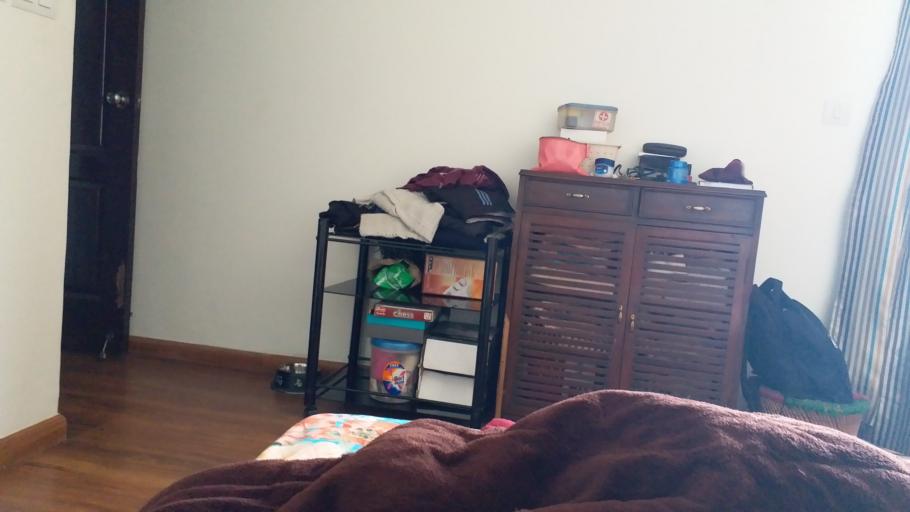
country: IN
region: Uttar Pradesh
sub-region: Gautam Buddha Nagar
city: Noida
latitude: 28.6409
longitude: 77.3662
